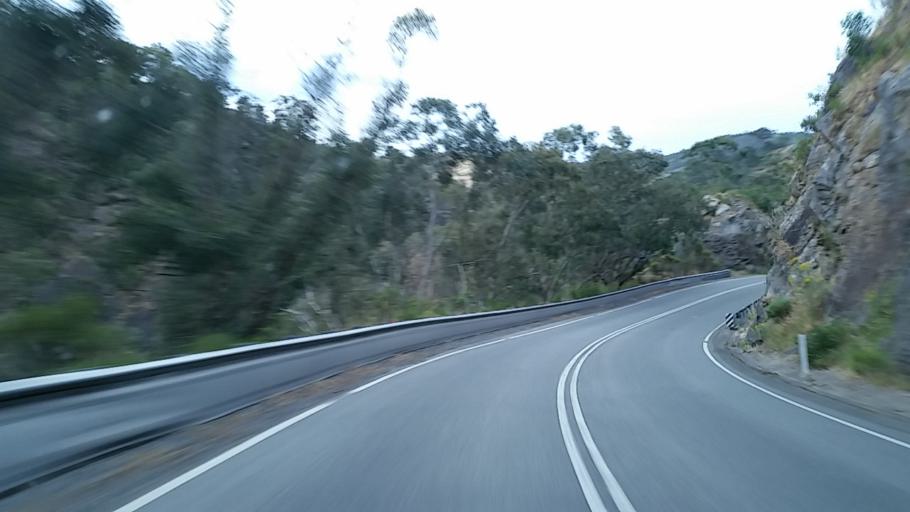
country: AU
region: South Australia
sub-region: Campbelltown
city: Athelstone
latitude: -34.8639
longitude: 138.7631
